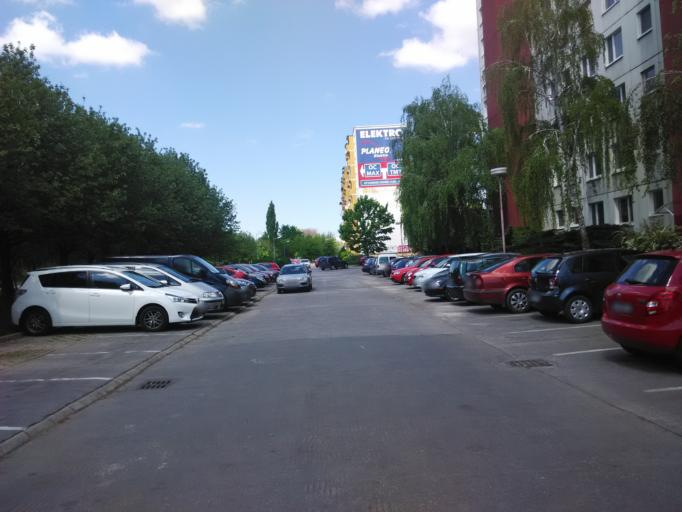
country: SK
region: Trnavsky
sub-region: Okres Trnava
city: Trnava
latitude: 48.3761
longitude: 17.5947
